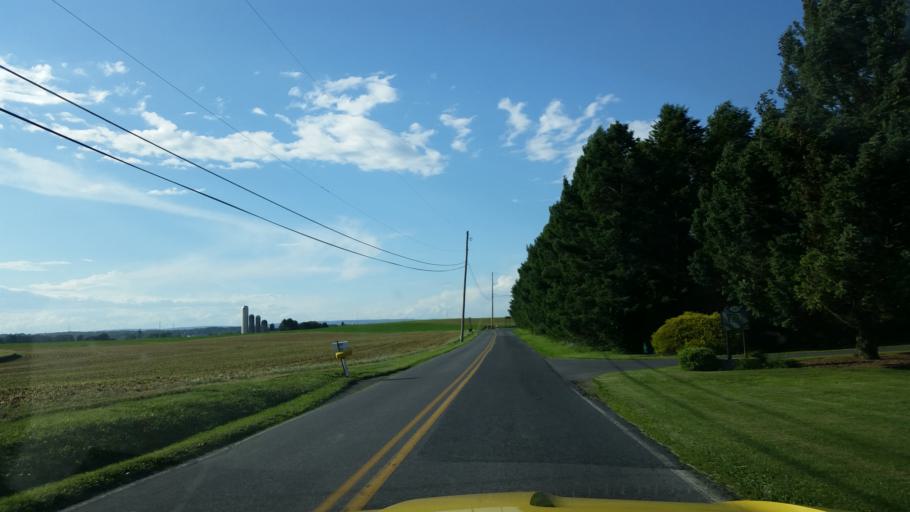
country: US
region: Pennsylvania
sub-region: Lebanon County
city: Avon
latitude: 40.3257
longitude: -76.3626
